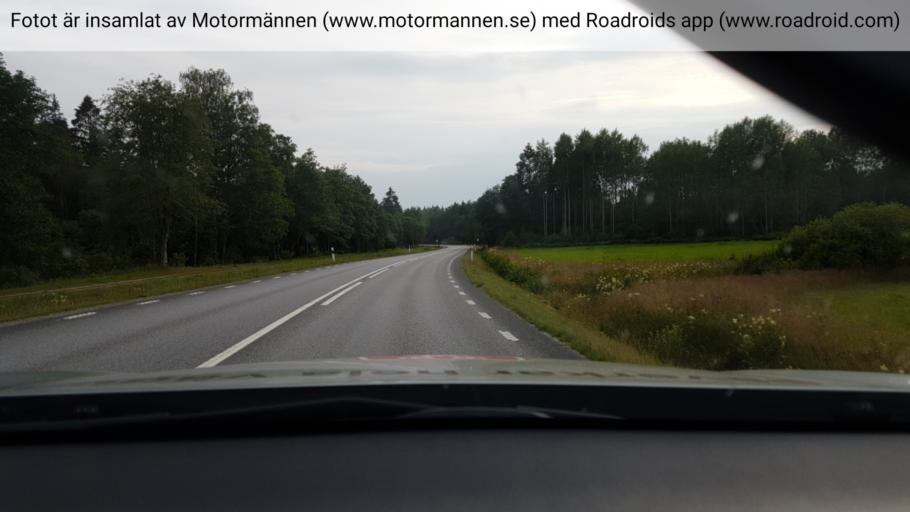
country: SE
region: Vaestra Goetaland
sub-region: Uddevalla Kommun
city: Uddevalla
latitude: 58.4069
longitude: 12.0064
